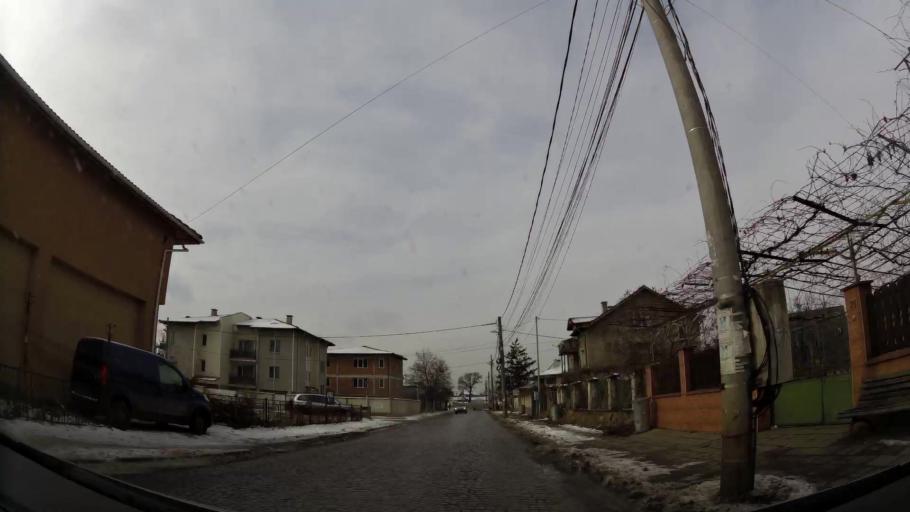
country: BG
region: Sofia-Capital
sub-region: Stolichna Obshtina
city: Sofia
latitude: 42.7135
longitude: 23.4161
